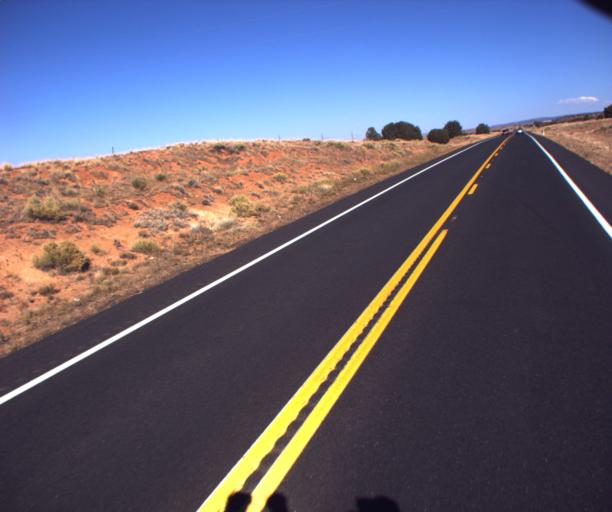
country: US
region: Arizona
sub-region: Coconino County
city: Kaibito
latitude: 36.4095
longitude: -110.8310
